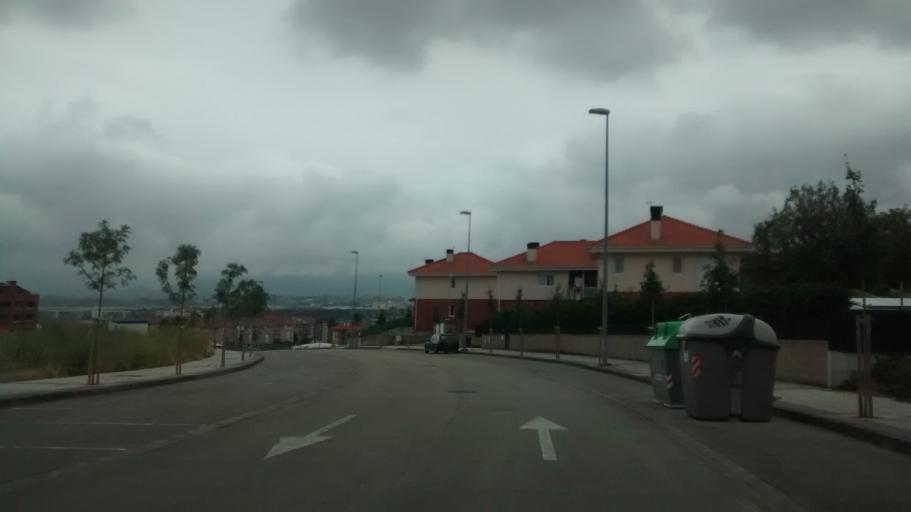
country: ES
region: Cantabria
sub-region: Provincia de Cantabria
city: Santa Cruz de Bezana
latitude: 43.4461
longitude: -3.8659
